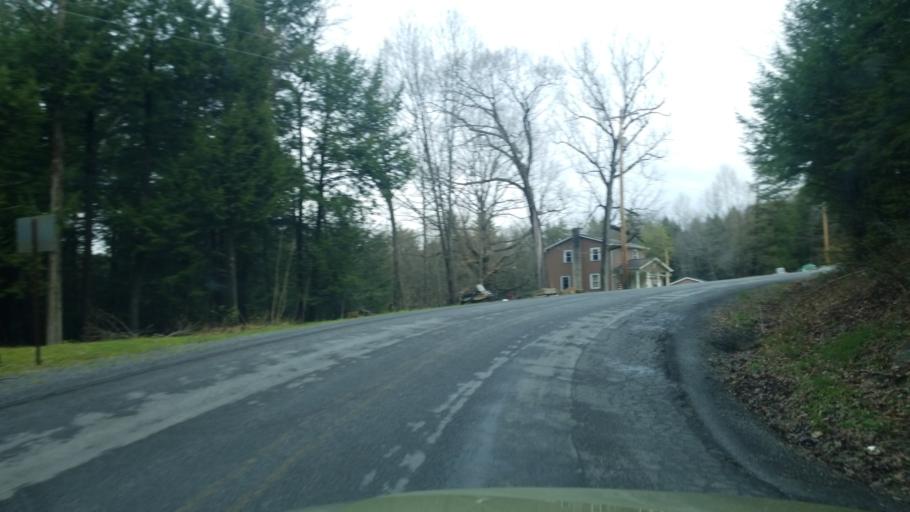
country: US
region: Pennsylvania
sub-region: Clearfield County
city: Clearfield
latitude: 41.0682
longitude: -78.4231
